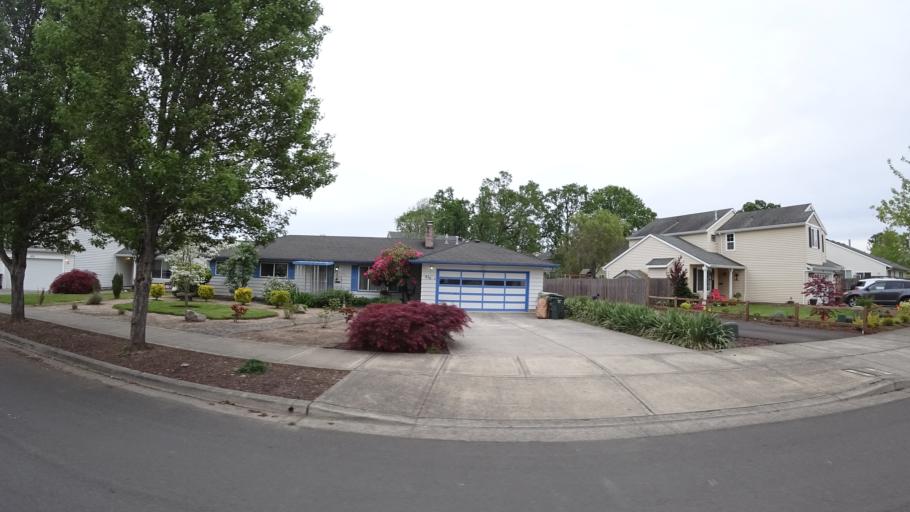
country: US
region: Oregon
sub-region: Washington County
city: Aloha
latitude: 45.5149
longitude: -122.9127
